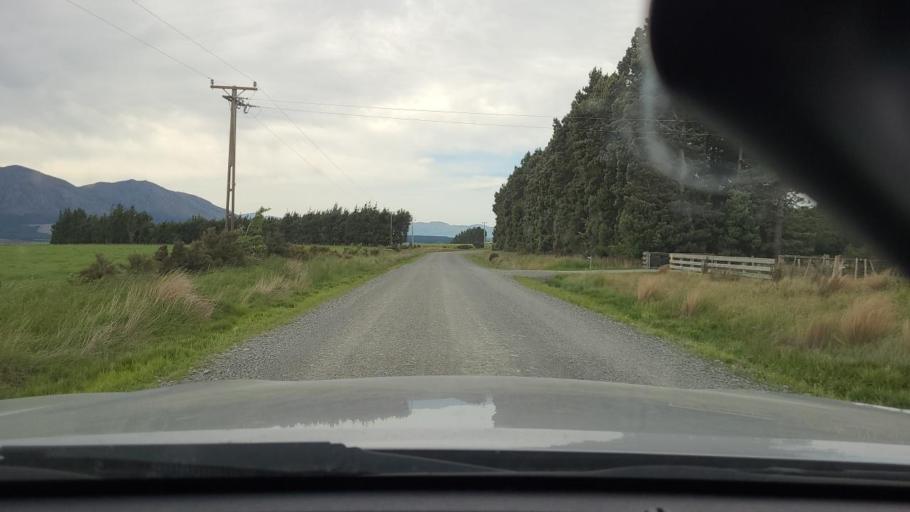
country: NZ
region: Southland
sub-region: Southland District
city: Te Anau
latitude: -45.6151
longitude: 168.1069
